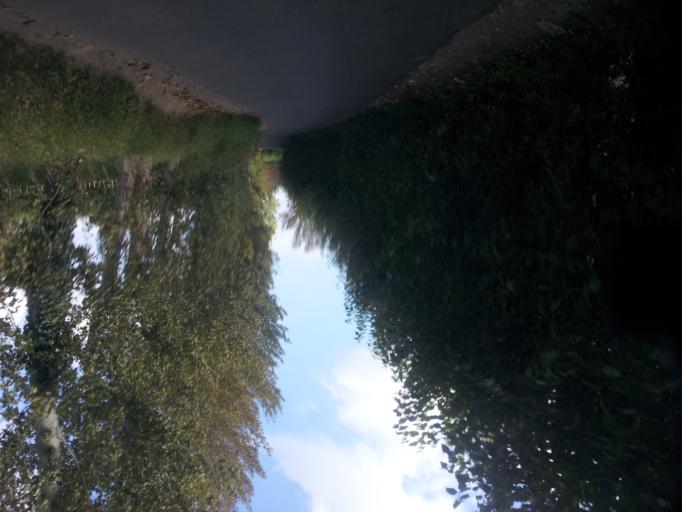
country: GB
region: England
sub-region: Kent
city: Strood
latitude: 51.4200
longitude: 0.4956
